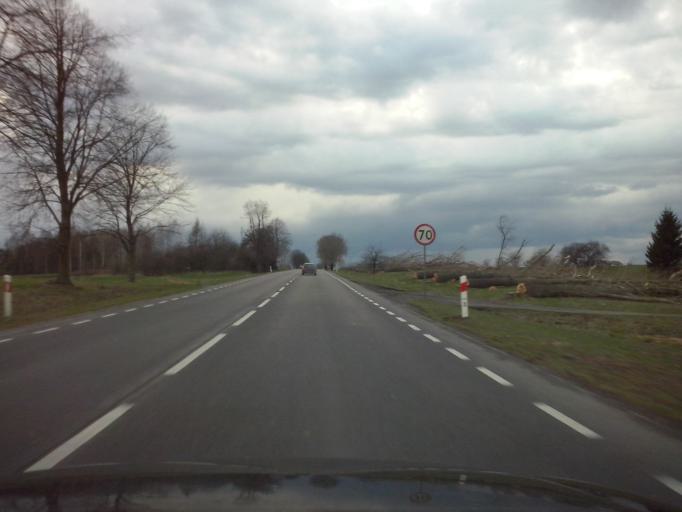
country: PL
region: Lublin Voivodeship
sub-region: Powiat chelmski
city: Rejowiec
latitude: 51.1684
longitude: 23.3433
